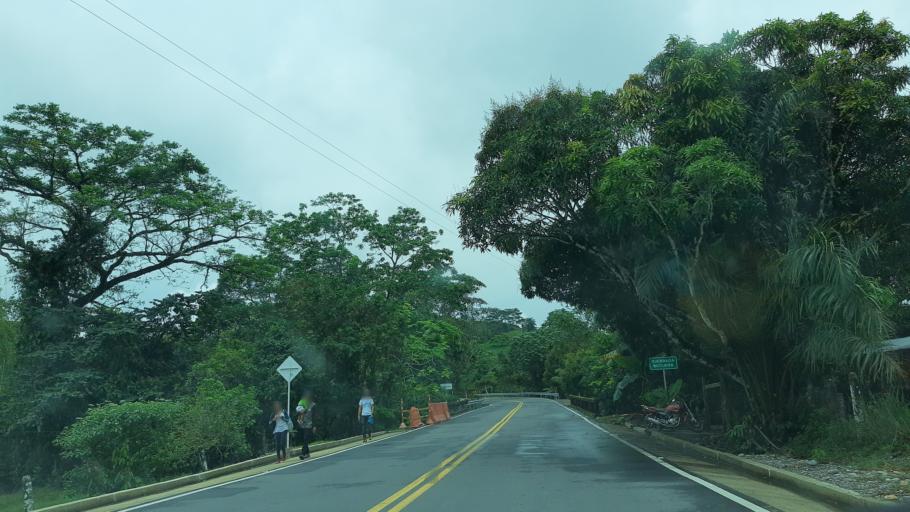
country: CO
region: Casanare
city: Sabanalarga
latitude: 4.7756
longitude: -73.0365
